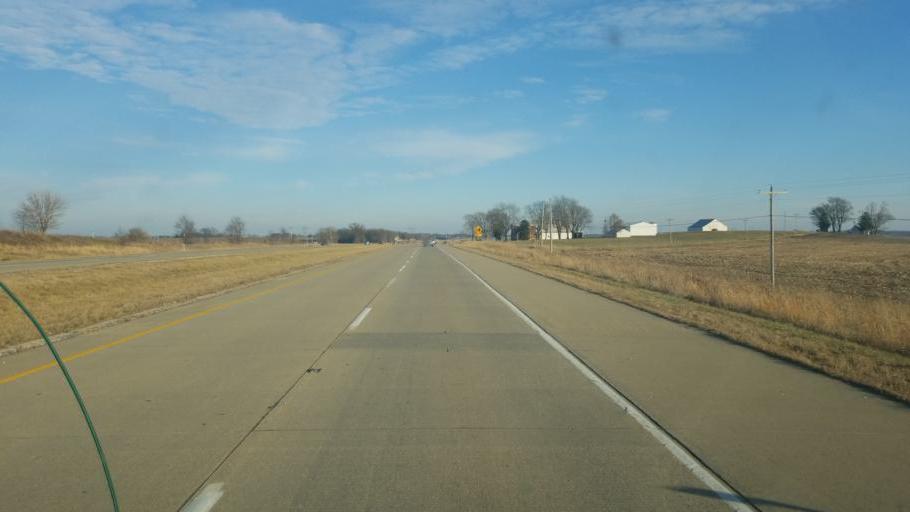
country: US
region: Indiana
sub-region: Knox County
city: Bicknell
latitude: 38.6735
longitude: -87.3616
